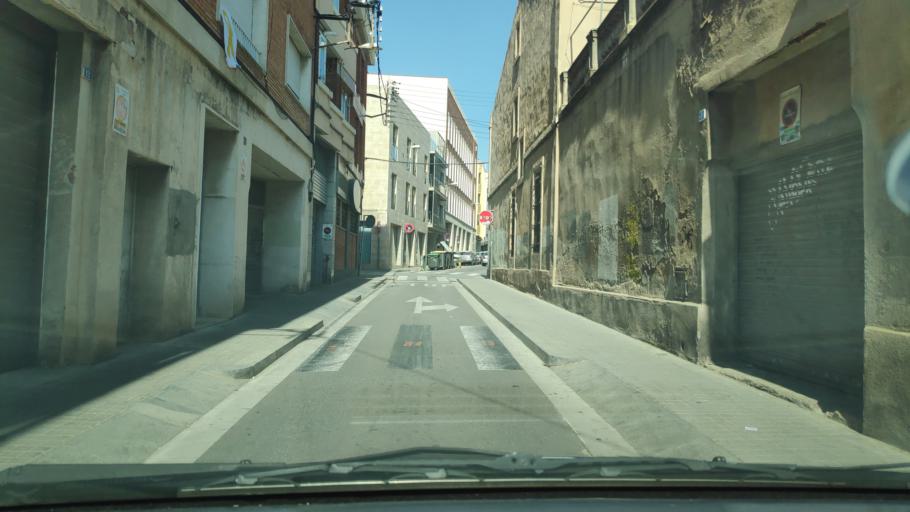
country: ES
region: Catalonia
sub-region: Provincia de Barcelona
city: Sabadell
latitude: 41.5439
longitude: 2.1114
